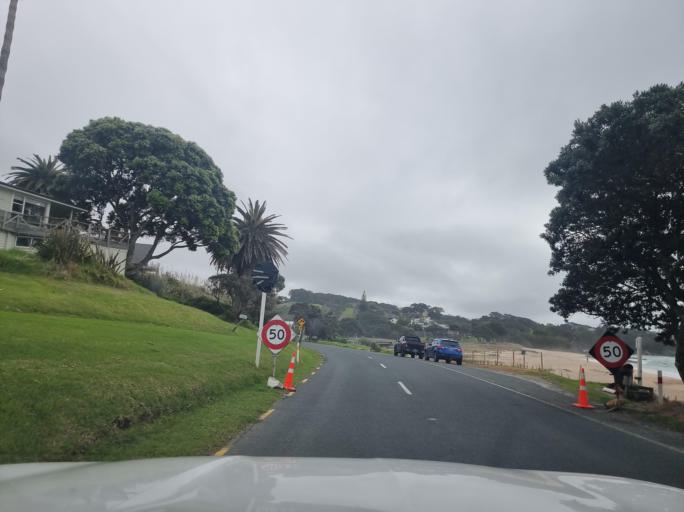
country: NZ
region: Northland
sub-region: Whangarei
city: Ruakaka
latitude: -36.0459
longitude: 174.5347
